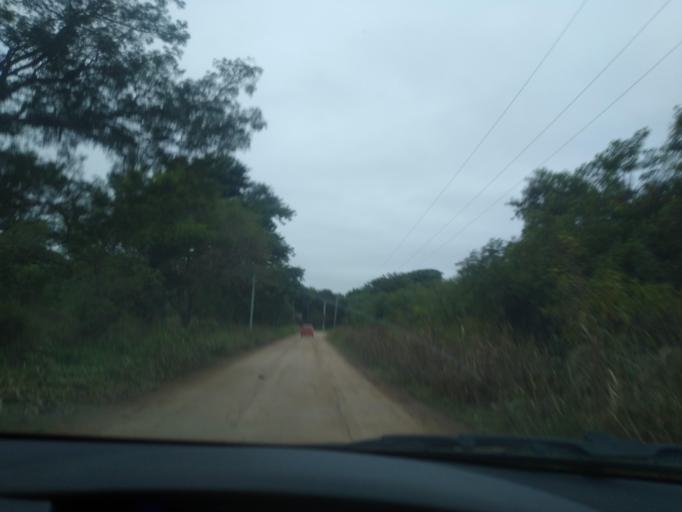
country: AR
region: Chaco
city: Colonia Benitez
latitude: -27.3354
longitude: -58.9598
